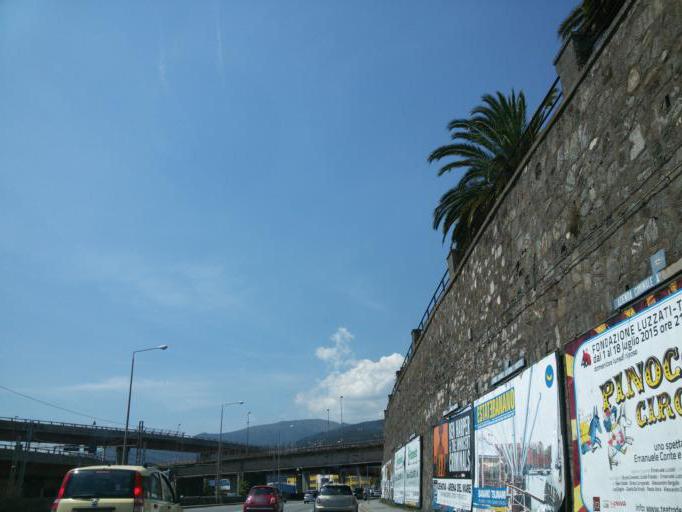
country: IT
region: Liguria
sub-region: Provincia di Genova
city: San Teodoro
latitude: 44.4165
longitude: 8.8604
